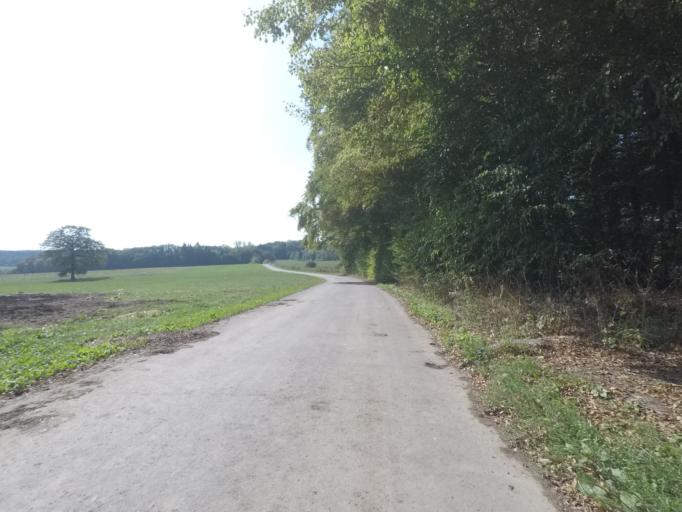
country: LU
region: Luxembourg
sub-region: Canton de Luxembourg
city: Olm
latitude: 49.6580
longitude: 6.0174
